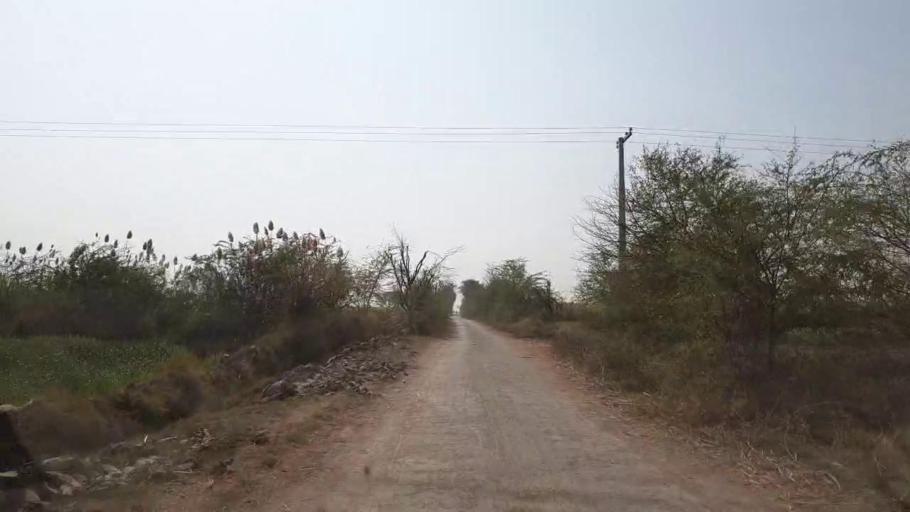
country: PK
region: Sindh
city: Mirpur Khas
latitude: 25.6037
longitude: 69.0246
